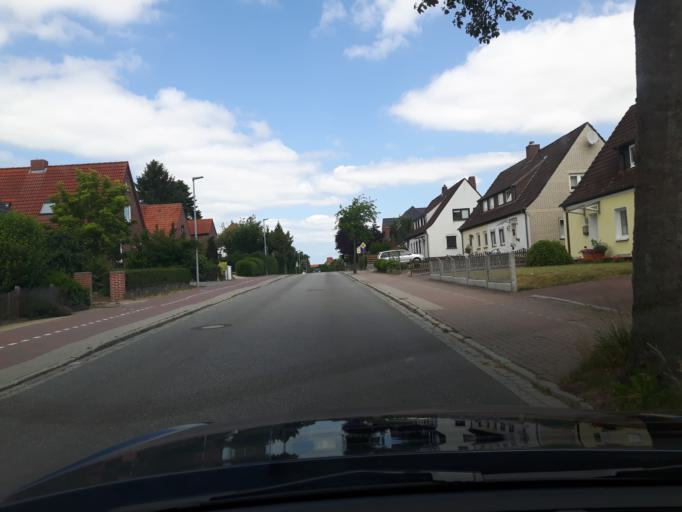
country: DE
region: Schleswig-Holstein
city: Neustadt in Holstein
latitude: 54.1028
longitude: 10.8212
